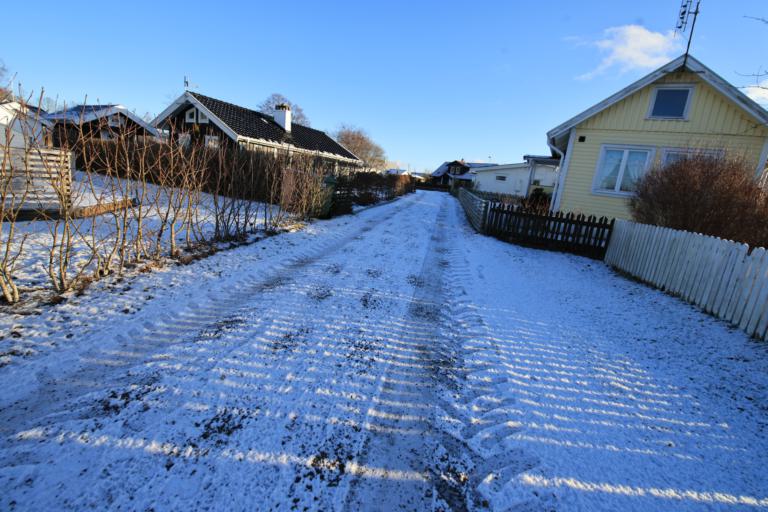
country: SE
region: Halland
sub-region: Varbergs Kommun
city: Traslovslage
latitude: 57.0638
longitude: 12.2862
